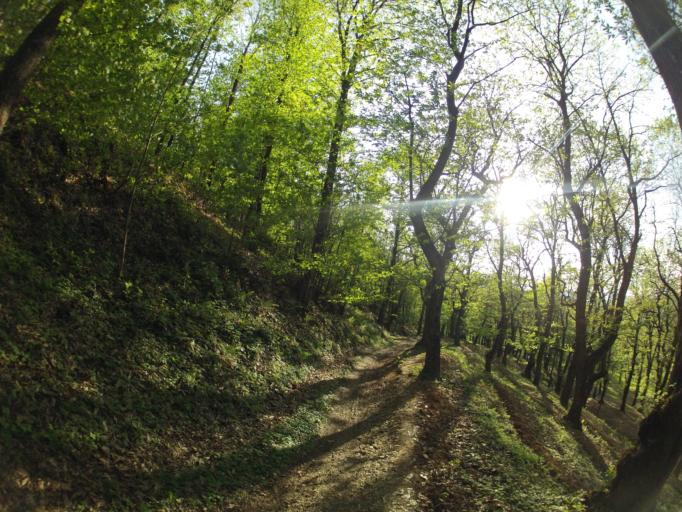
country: IT
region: Piedmont
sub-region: Provincia di Cuneo
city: Boves
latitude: 44.3142
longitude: 7.5809
